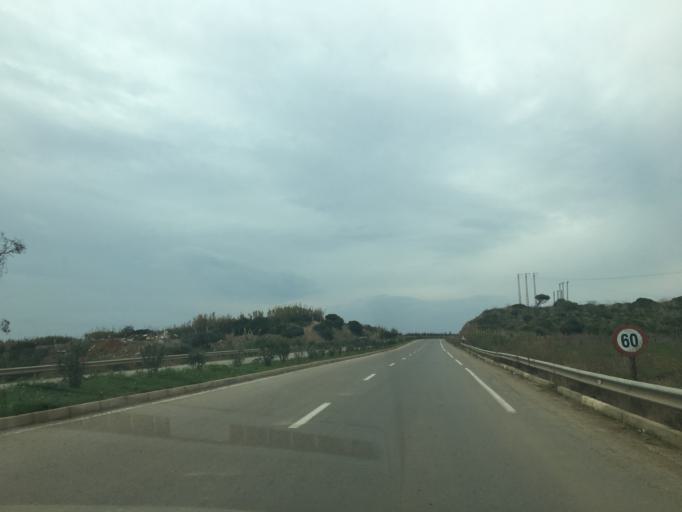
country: DZ
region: Tipaza
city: Hadjout
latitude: 36.6226
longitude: 2.2638
